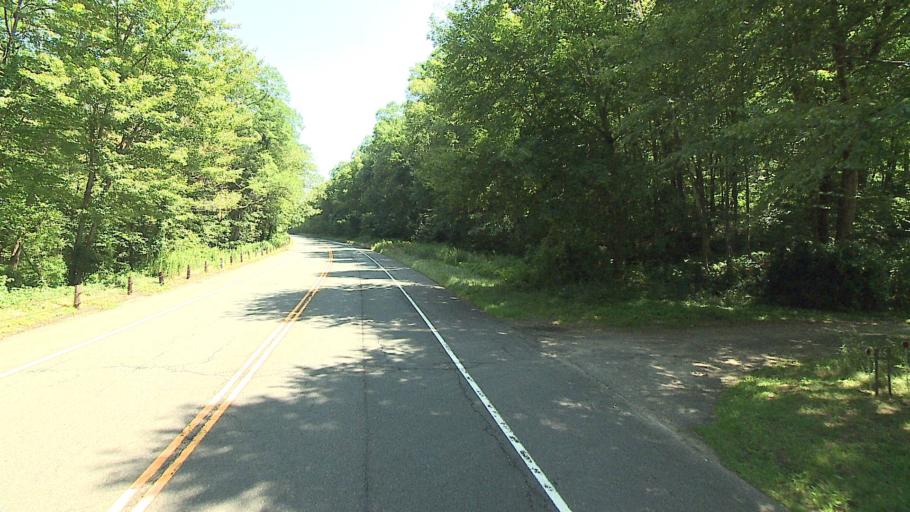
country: US
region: Connecticut
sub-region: Hartford County
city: Collinsville
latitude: 41.7773
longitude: -72.9183
